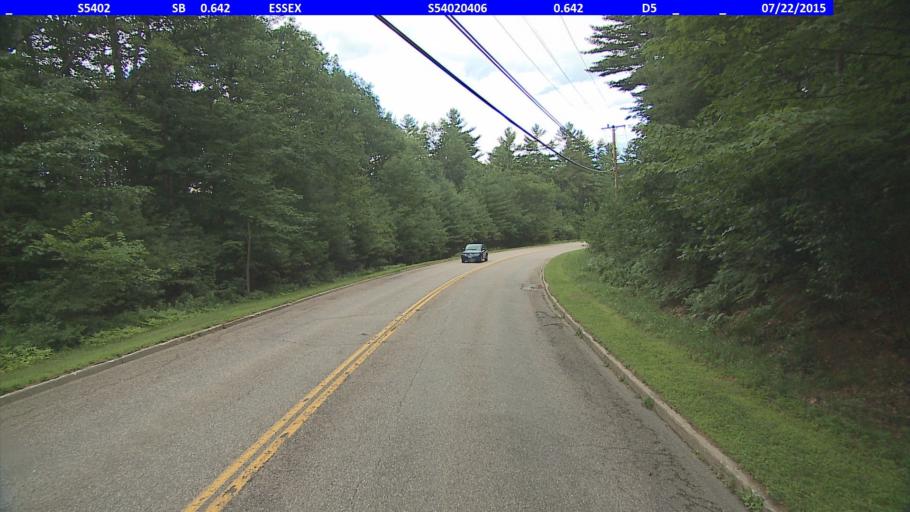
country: US
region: Vermont
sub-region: Chittenden County
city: Williston
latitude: 44.4879
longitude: -73.0495
